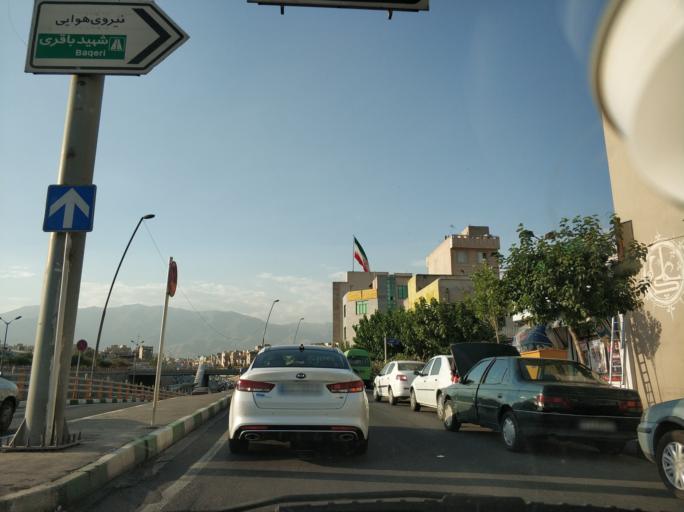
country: IR
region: Tehran
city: Tehran
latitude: 35.7025
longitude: 51.4579
